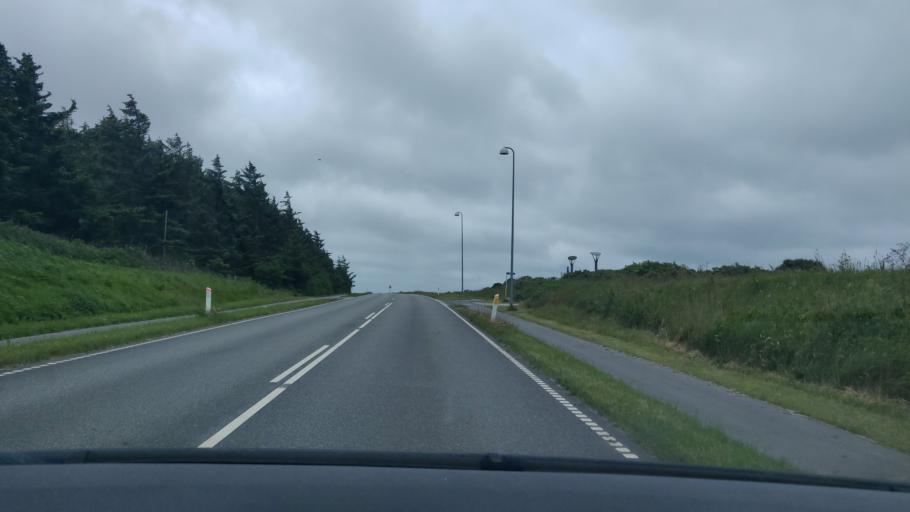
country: DK
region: North Denmark
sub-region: Hjorring Kommune
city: Hirtshals
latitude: 57.5849
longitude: 9.9524
